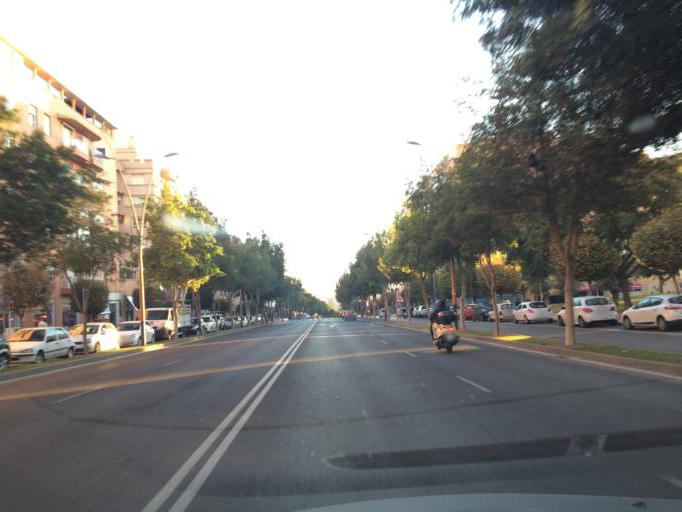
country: ES
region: Andalusia
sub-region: Provincia de Almeria
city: Almeria
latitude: 36.8501
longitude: -2.4466
